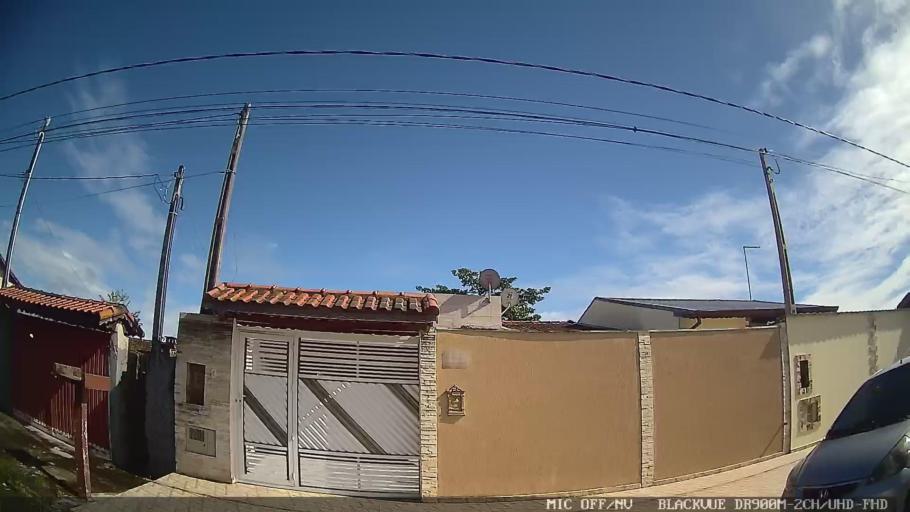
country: BR
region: Sao Paulo
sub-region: Itanhaem
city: Itanhaem
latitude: -24.2385
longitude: -46.8962
